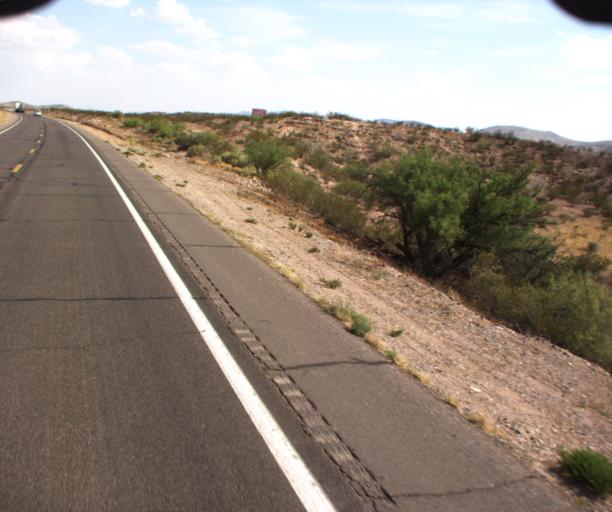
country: US
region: Arizona
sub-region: Greenlee County
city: Clifton
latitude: 32.7846
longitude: -109.1590
